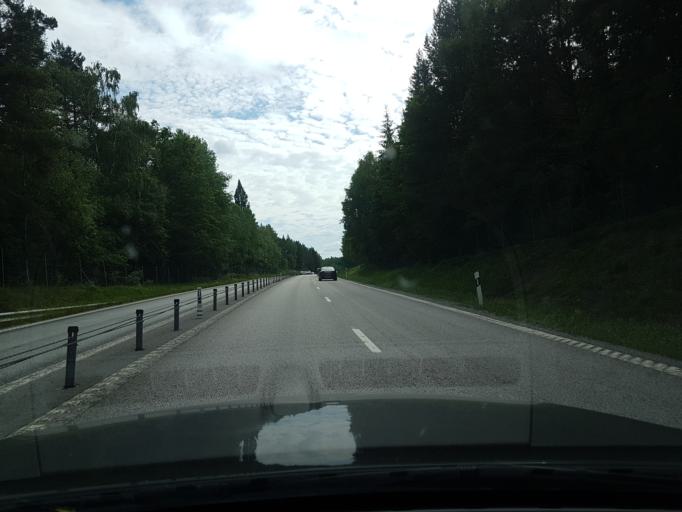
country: SE
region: Stockholm
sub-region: Osterakers Kommun
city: Akersberga
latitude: 59.5538
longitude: 18.2299
